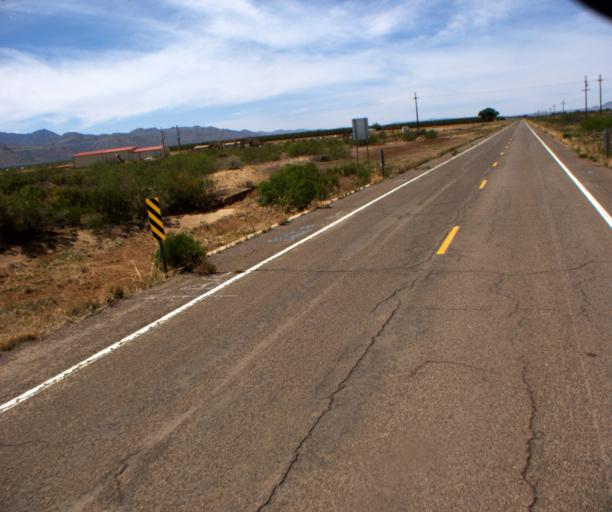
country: US
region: Arizona
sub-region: Cochise County
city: Willcox
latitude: 32.3211
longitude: -109.4557
